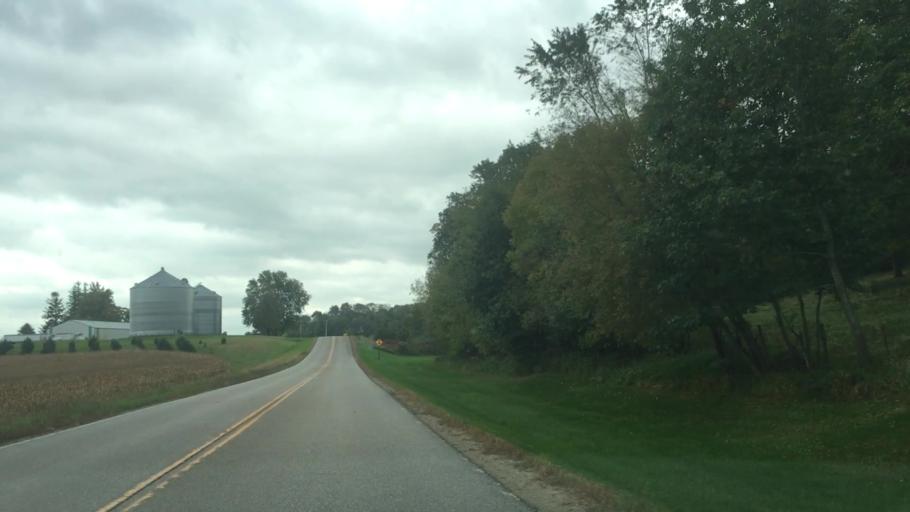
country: US
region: Minnesota
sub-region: Fillmore County
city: Preston
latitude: 43.7363
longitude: -92.0064
